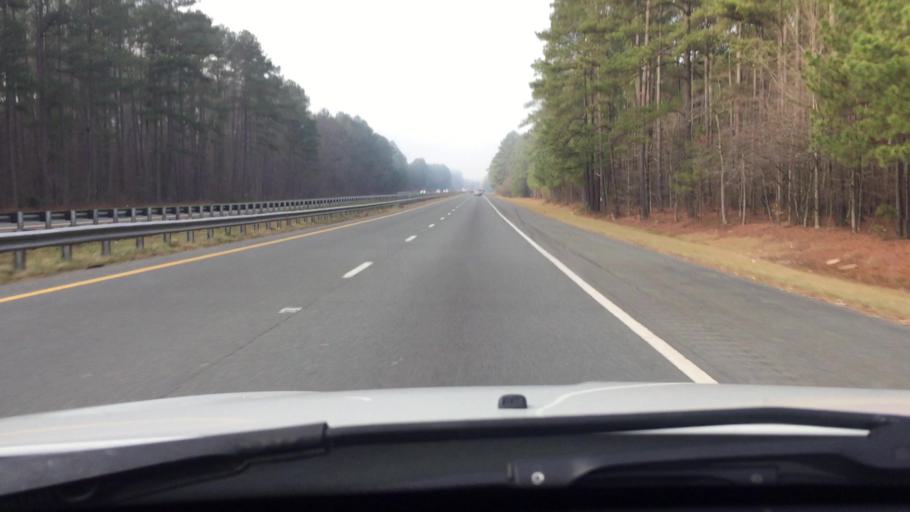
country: US
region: North Carolina
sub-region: Chatham County
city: Pittsboro
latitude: 35.6427
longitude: -79.0248
